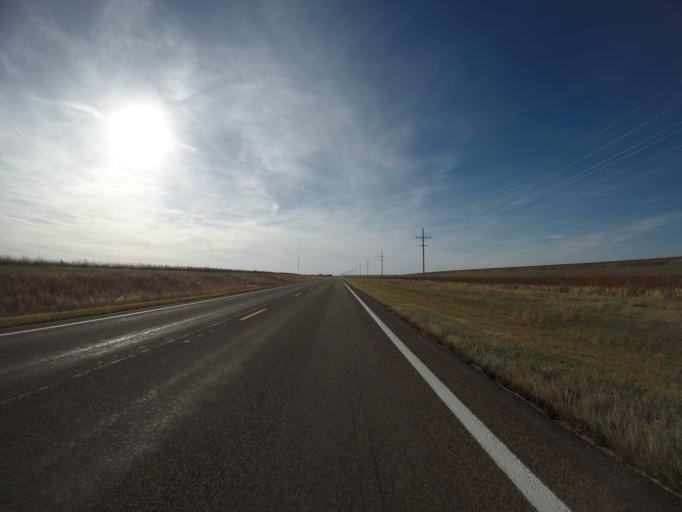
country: US
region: Kansas
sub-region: Rawlins County
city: Atwood
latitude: 39.7854
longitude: -101.2523
